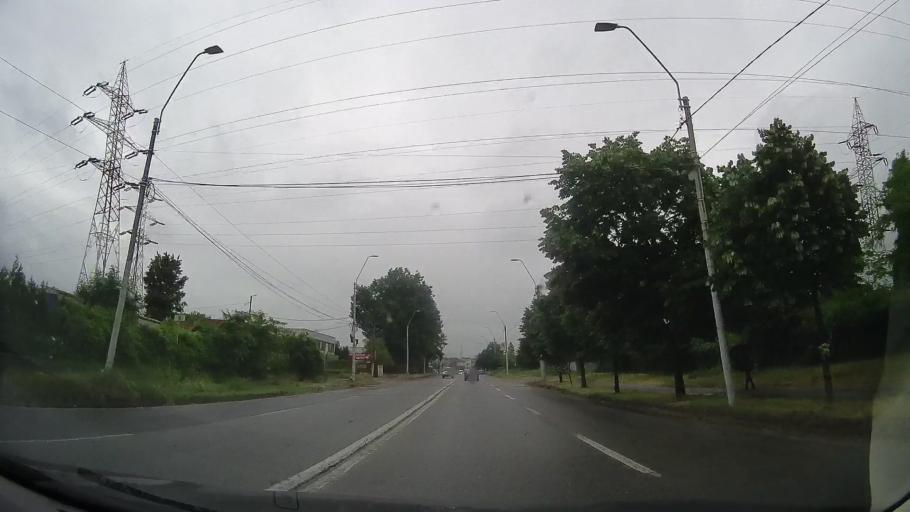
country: RS
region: Central Serbia
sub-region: Borski Okrug
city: Kladovo
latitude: 44.6240
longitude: 22.6290
